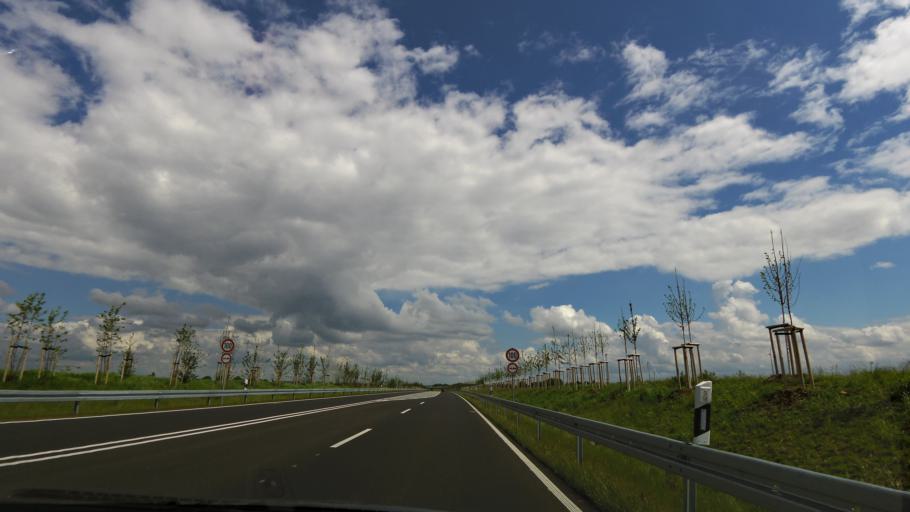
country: DE
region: North Rhine-Westphalia
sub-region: Regierungsbezirk Koln
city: Heinsberg
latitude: 51.0216
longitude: 6.0747
